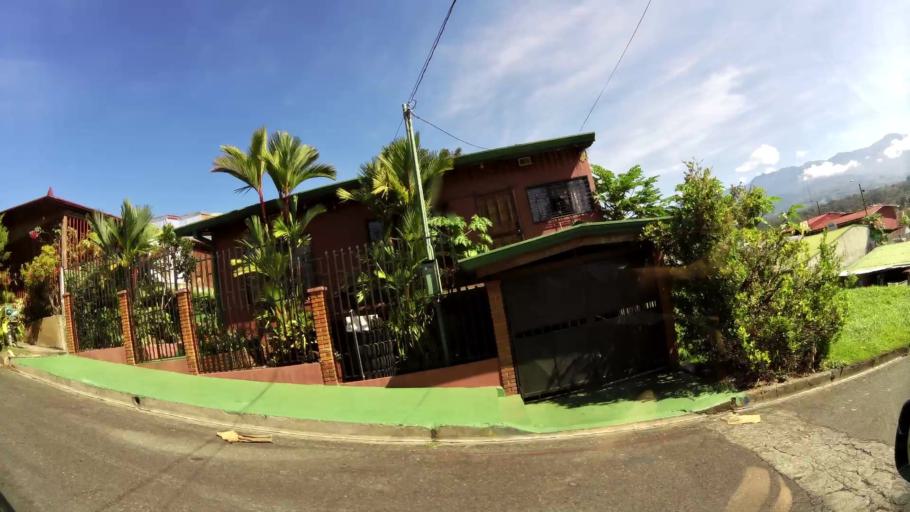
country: CR
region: San Jose
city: San Isidro
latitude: 9.3751
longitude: -83.7071
